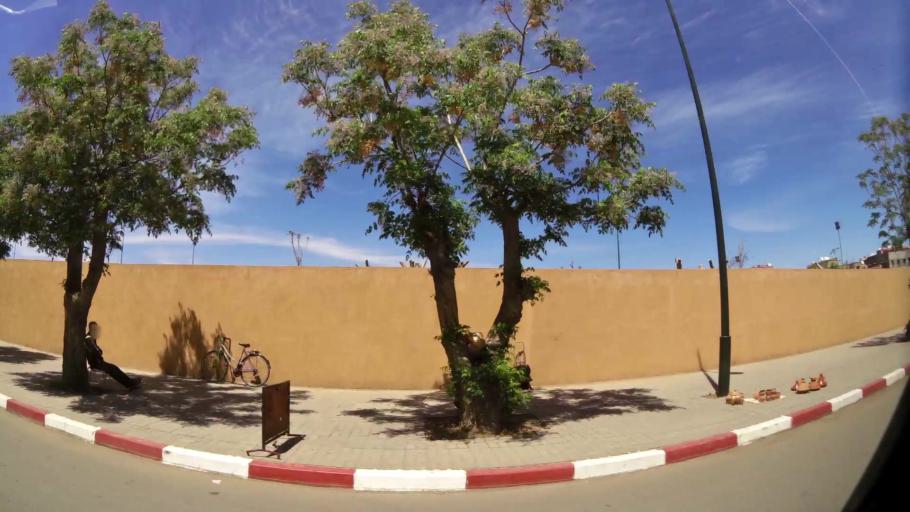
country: MA
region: Marrakech-Tensift-Al Haouz
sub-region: Marrakech
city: Marrakesh
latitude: 31.6547
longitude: -7.9970
